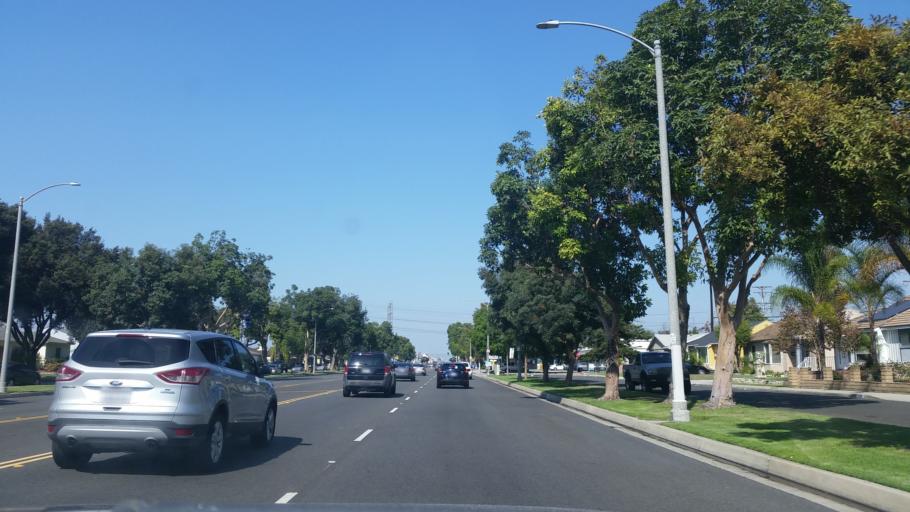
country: US
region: California
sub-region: Los Angeles County
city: Lakewood
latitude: 33.8644
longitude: -118.1251
